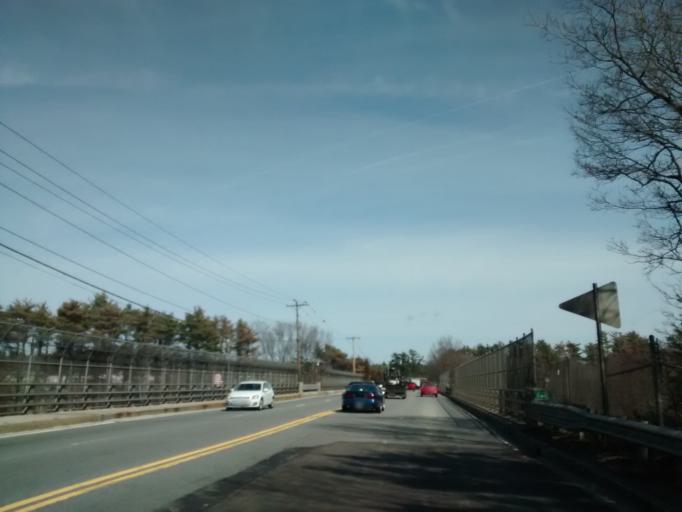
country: US
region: Massachusetts
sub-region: Norfolk County
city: Bellingham
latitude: 42.1142
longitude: -71.4669
